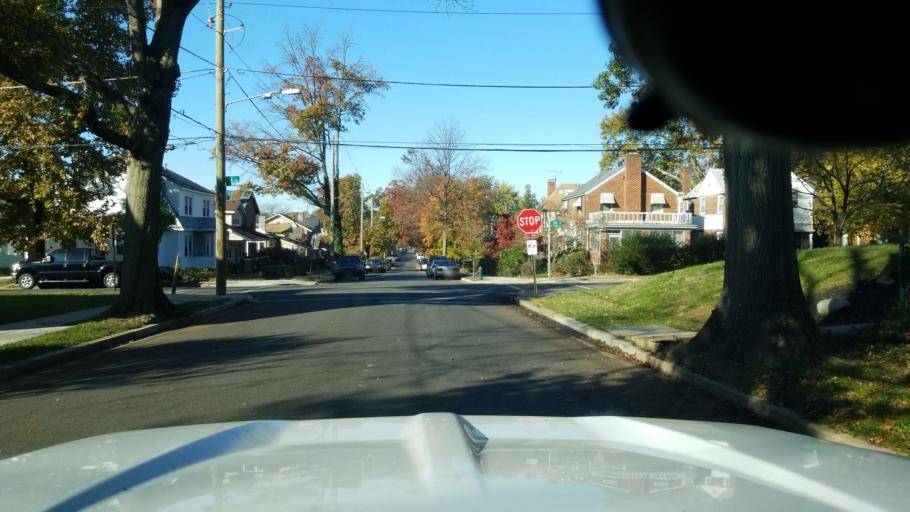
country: US
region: Maryland
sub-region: Prince George's County
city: Mount Rainier
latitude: 38.9351
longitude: -76.9698
